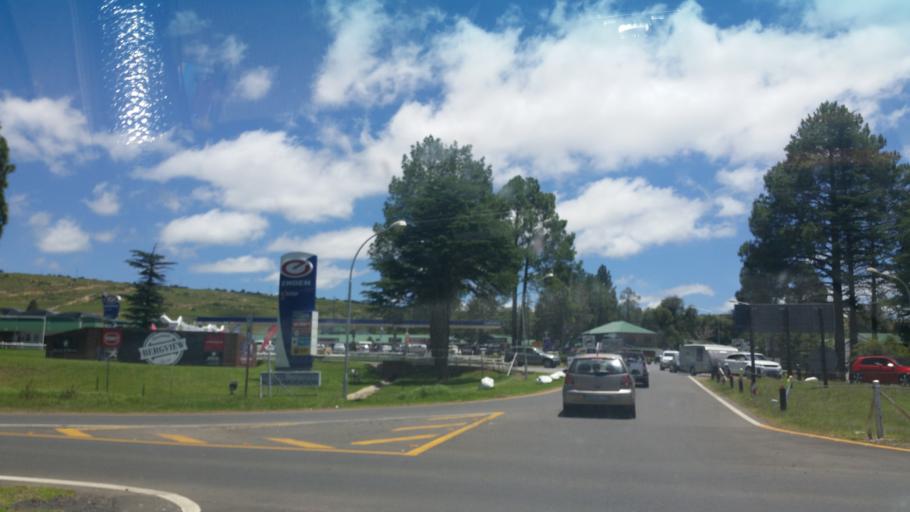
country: ZA
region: Orange Free State
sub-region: Thabo Mofutsanyana District Municipality
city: Harrismith
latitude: -28.2565
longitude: 29.1162
